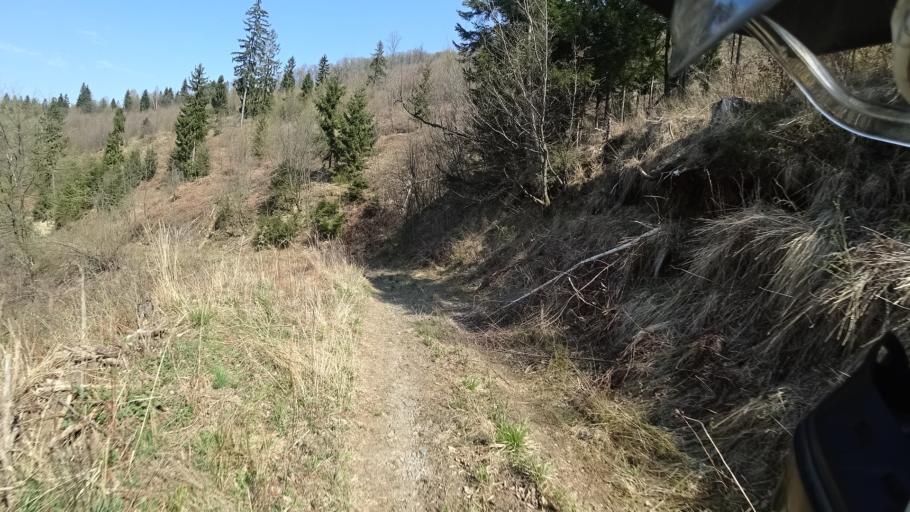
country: HR
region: Zagrebacka
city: Jablanovec
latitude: 45.8896
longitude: 15.9178
